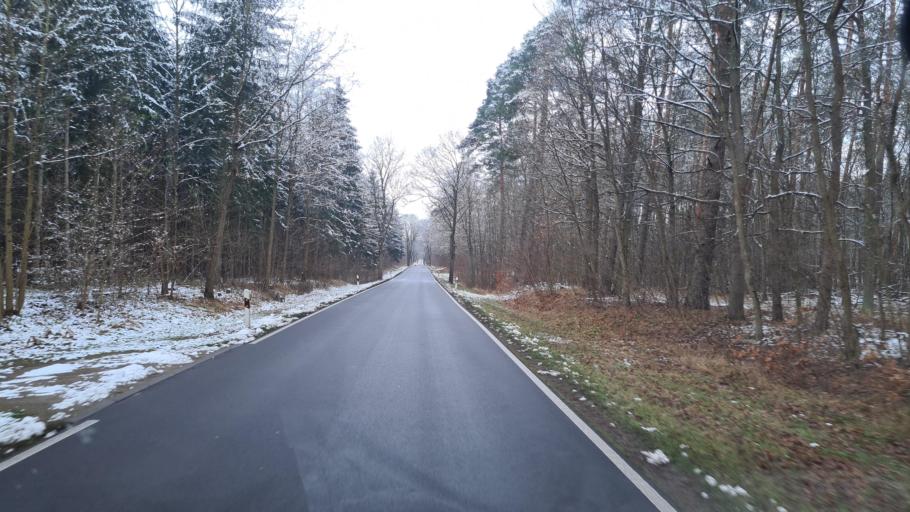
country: DE
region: Brandenburg
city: Strausberg
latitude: 52.5526
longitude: 13.9159
